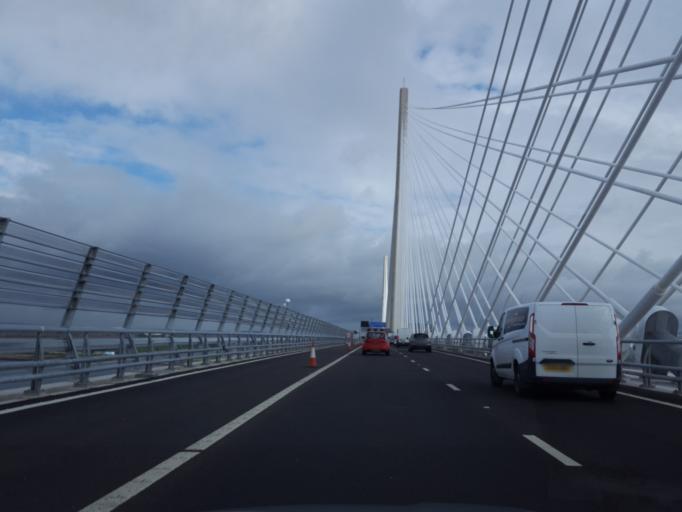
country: GB
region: Scotland
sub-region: Edinburgh
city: Queensferry
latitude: 56.0016
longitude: -3.4150
